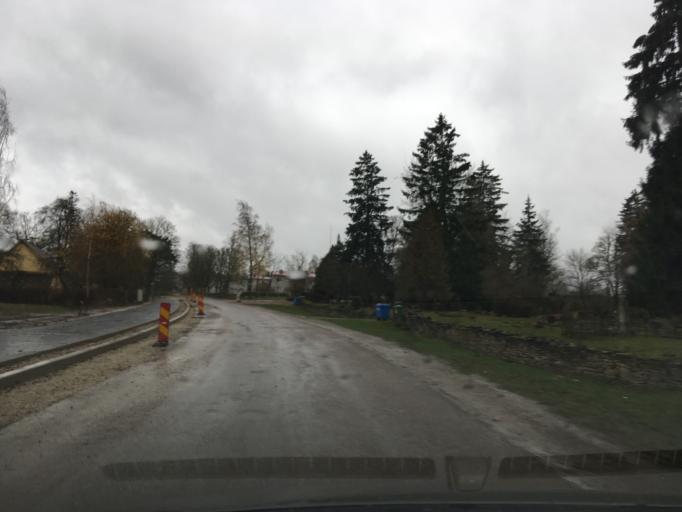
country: EE
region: Laeaene
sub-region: Lihula vald
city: Lihula
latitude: 58.6799
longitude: 23.8235
